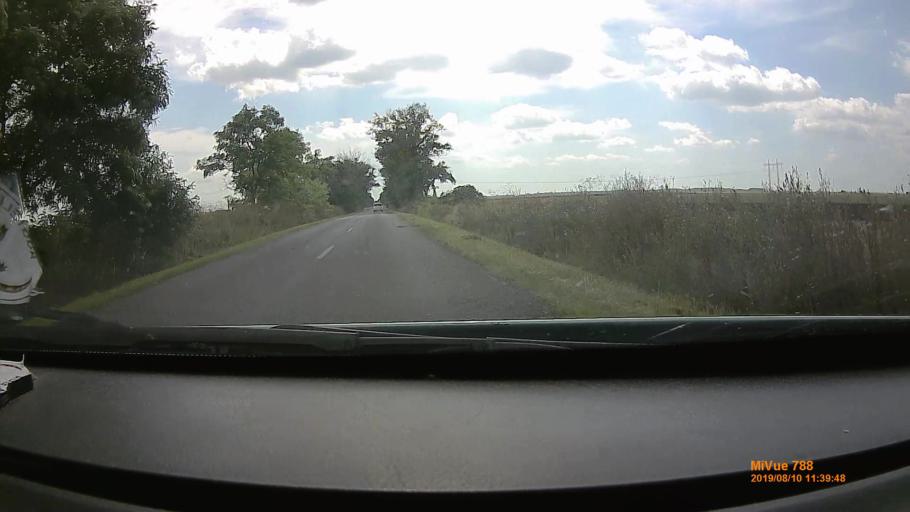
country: HU
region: Borsod-Abauj-Zemplen
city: Mezokovesd
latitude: 47.7669
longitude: 20.5963
